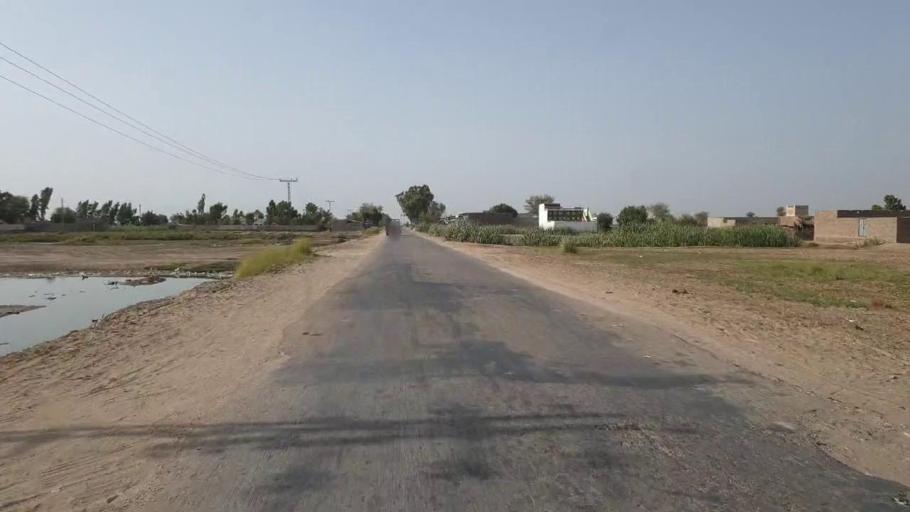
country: PK
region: Sindh
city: Sanghar
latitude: 26.2880
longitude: 68.9309
